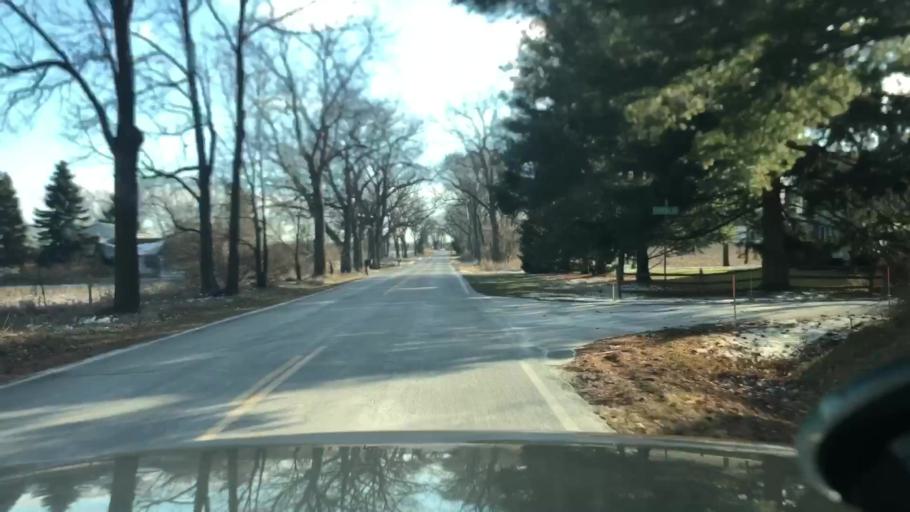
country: US
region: Michigan
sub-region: Jackson County
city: Vandercook Lake
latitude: 42.1716
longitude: -84.4521
